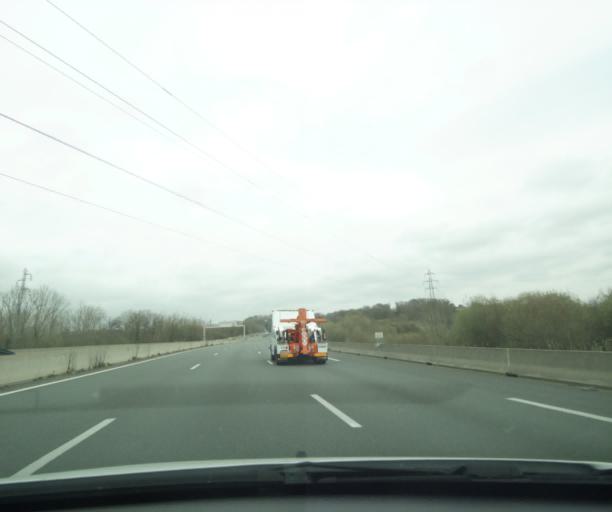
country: FR
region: Aquitaine
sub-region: Departement des Pyrenees-Atlantiques
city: Bayonne
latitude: 43.4691
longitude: -1.4755
